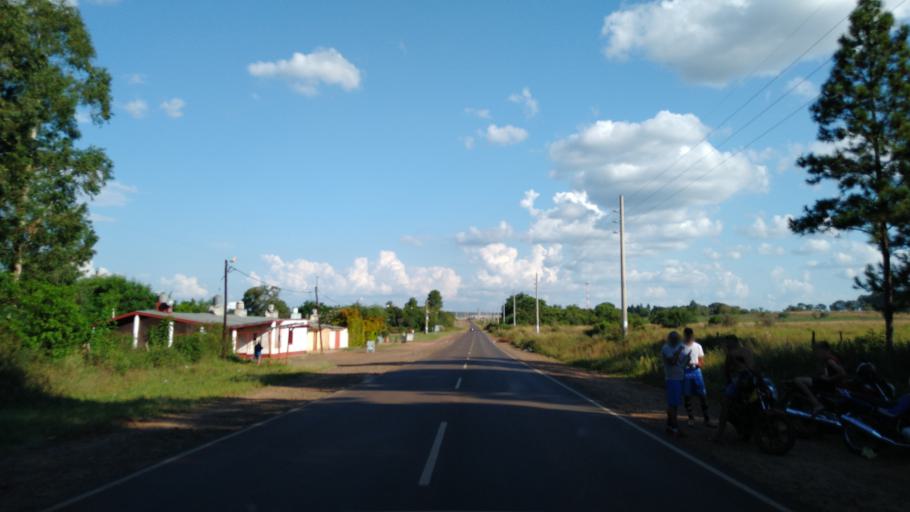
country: PY
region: Itapua
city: San Juan del Parana
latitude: -27.3839
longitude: -55.9915
